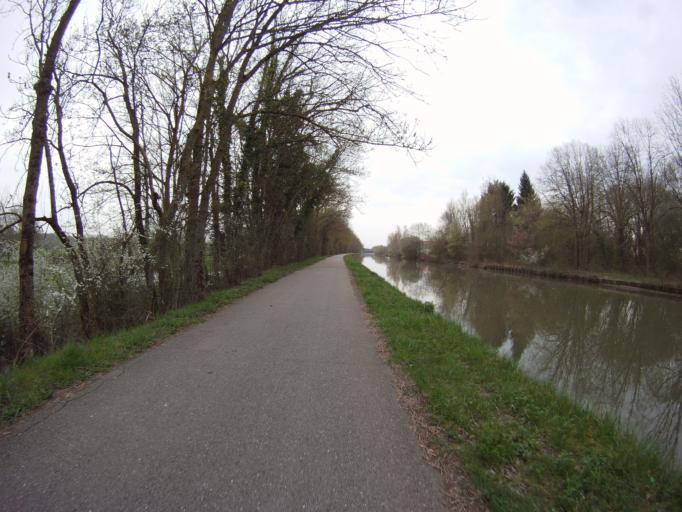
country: FR
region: Lorraine
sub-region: Departement de Meurthe-et-Moselle
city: Laneuveville-devant-Nancy
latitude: 48.6647
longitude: 6.2218
